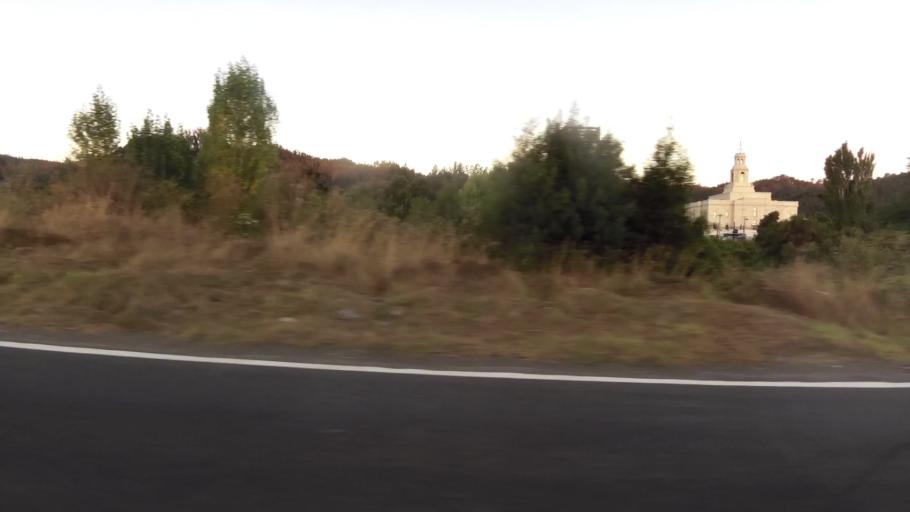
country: CL
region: Biobio
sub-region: Provincia de Concepcion
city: Concepcion
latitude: -36.8510
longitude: -73.0529
